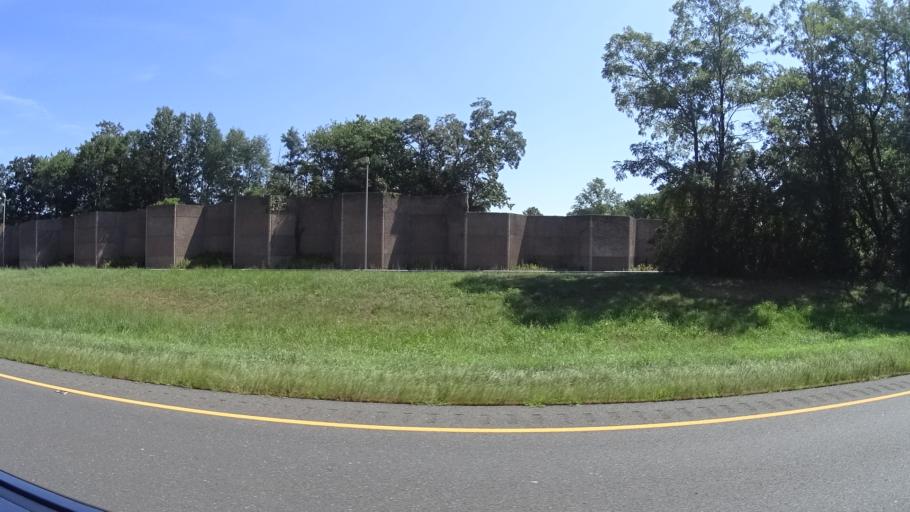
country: US
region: New Jersey
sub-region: Monmouth County
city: Wanamassa
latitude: 40.2471
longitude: -74.0549
